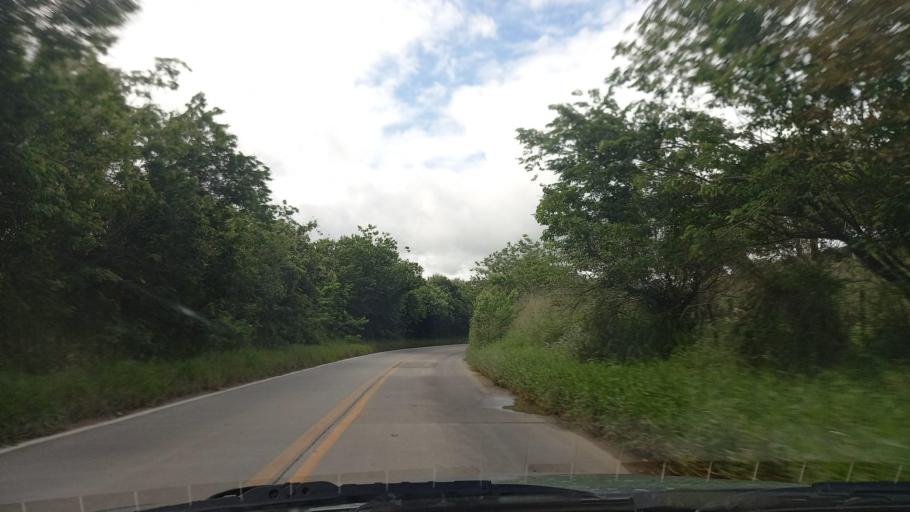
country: BR
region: Pernambuco
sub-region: Quipapa
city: Quipapa
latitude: -8.7787
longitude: -35.9475
